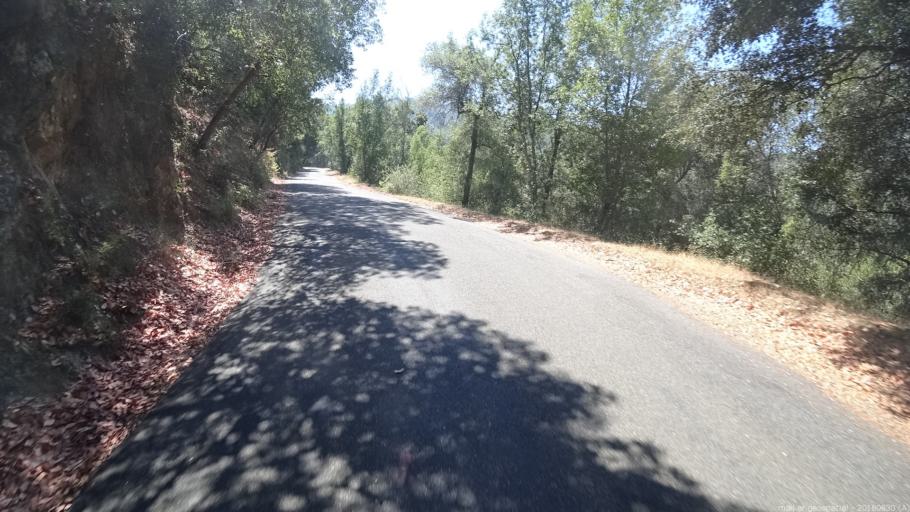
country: US
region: California
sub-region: Monterey County
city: Greenfield
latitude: 36.0153
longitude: -121.4310
